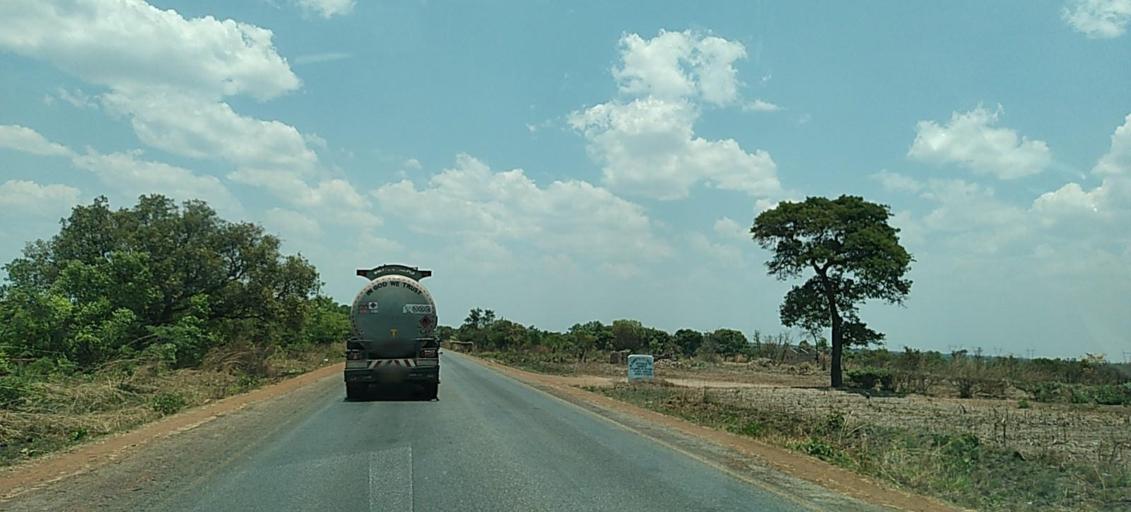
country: ZM
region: Central
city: Kapiri Mposhi
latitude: -13.7828
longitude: 28.6460
